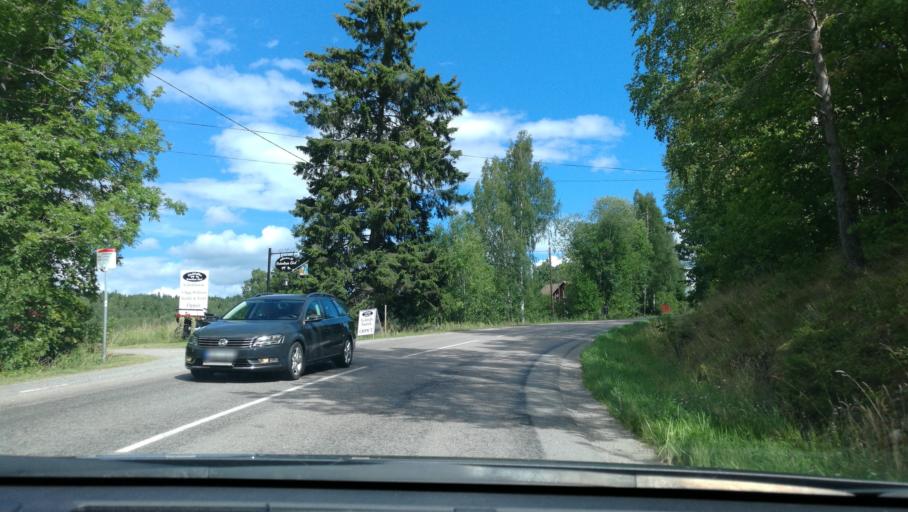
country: SE
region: OEstergoetland
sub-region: Norrkopings Kommun
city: Krokek
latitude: 58.6678
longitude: 16.4104
